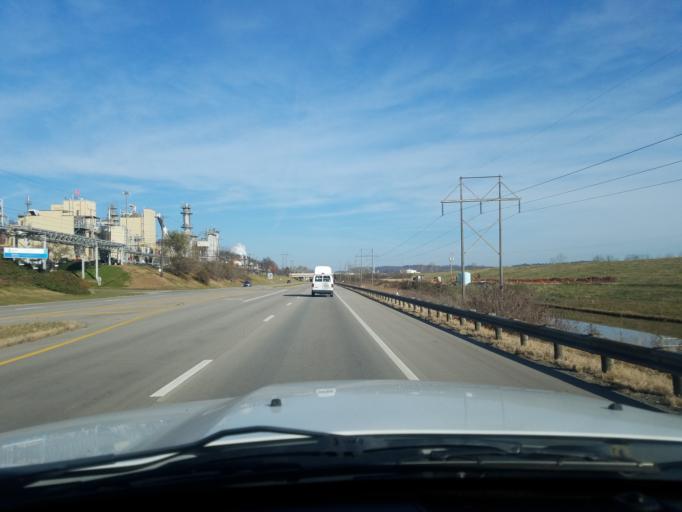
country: US
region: West Virginia
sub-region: Wood County
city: Boaz
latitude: 39.3700
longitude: -81.5161
